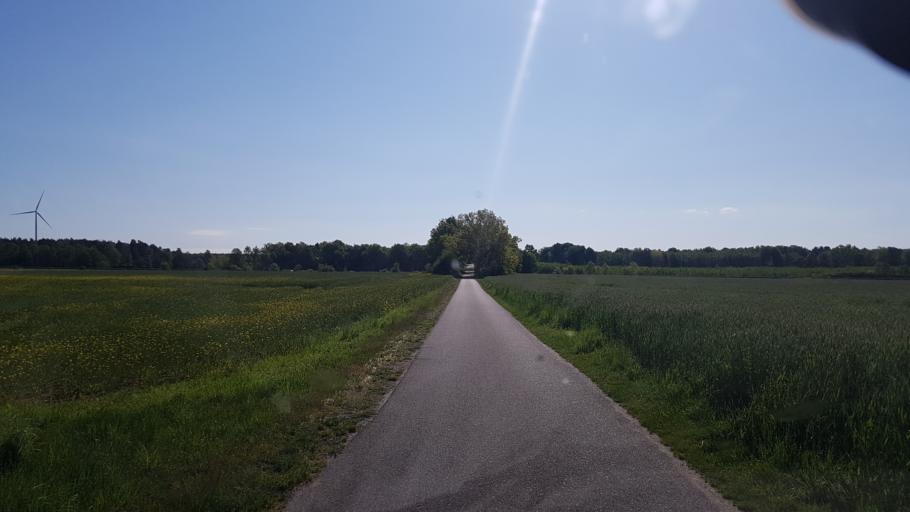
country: DE
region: Brandenburg
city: Grossraschen
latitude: 51.5987
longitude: 13.9469
